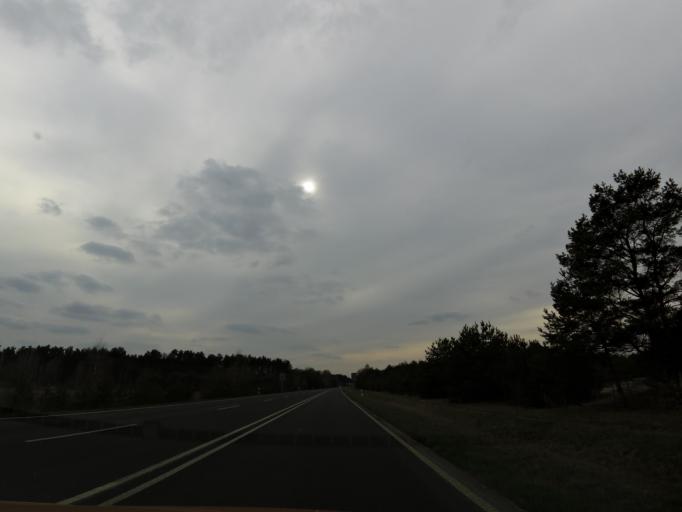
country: DE
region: Brandenburg
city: Mullrose
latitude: 52.2641
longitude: 14.4219
